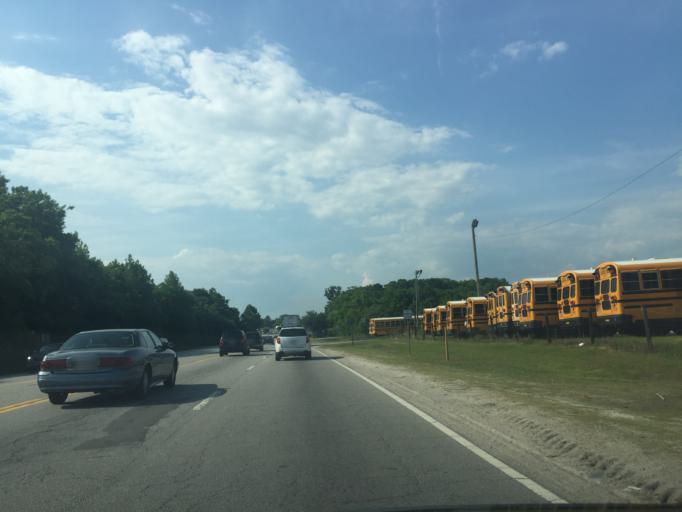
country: US
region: Georgia
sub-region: Chatham County
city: Garden City
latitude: 32.0812
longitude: -81.1573
